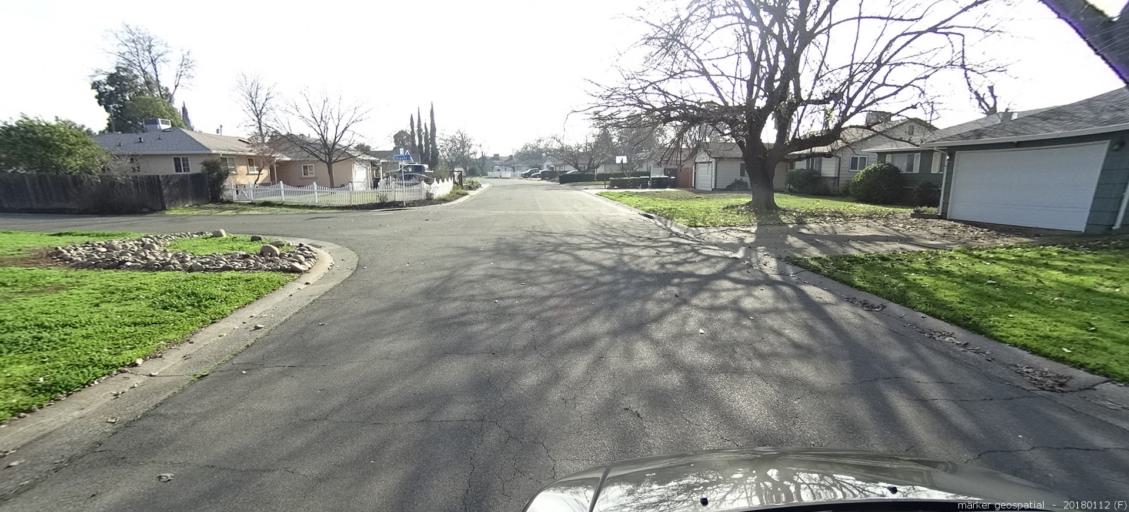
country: US
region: California
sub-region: Sacramento County
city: Rancho Cordova
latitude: 38.5983
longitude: -121.2924
